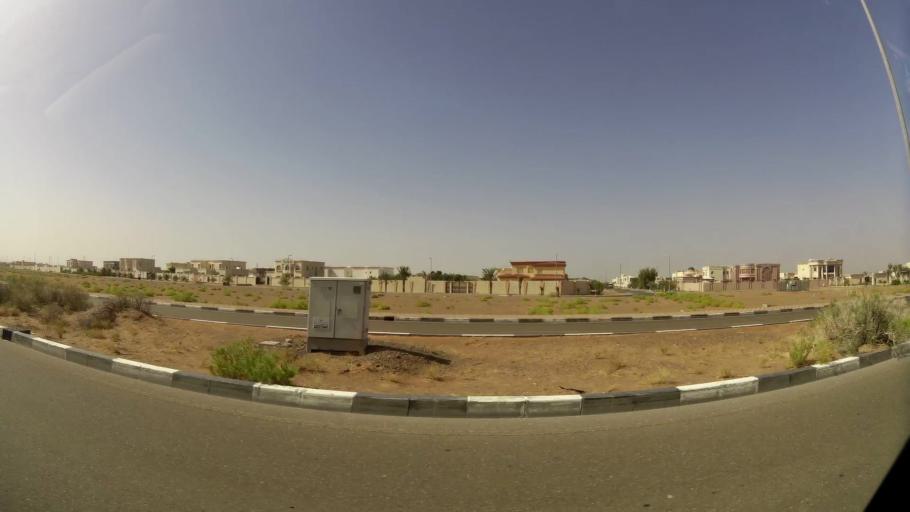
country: OM
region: Al Buraimi
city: Al Buraymi
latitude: 24.3449
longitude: 55.7839
